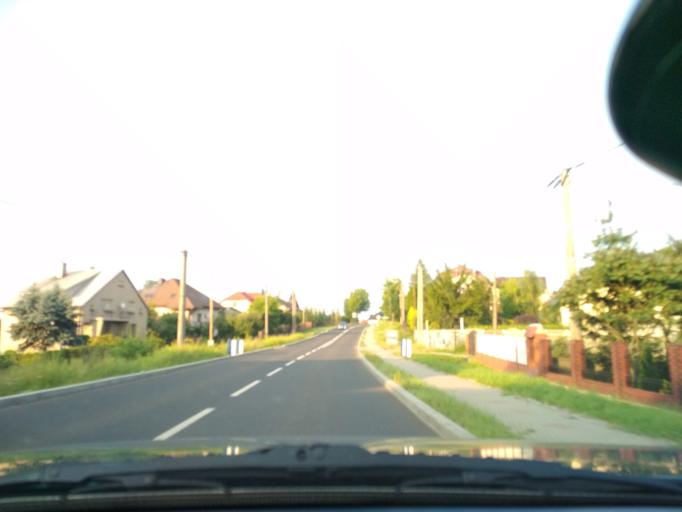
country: PL
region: Silesian Voivodeship
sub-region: Powiat zawiercianski
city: Ogrodzieniec
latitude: 50.4584
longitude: 19.5576
